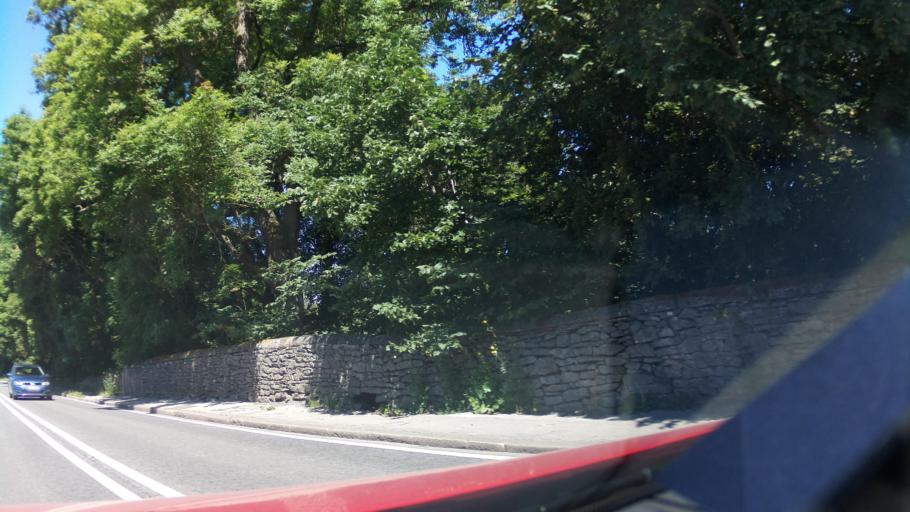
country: GB
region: England
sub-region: Derbyshire
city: Bakewell
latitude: 53.1897
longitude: -1.6467
